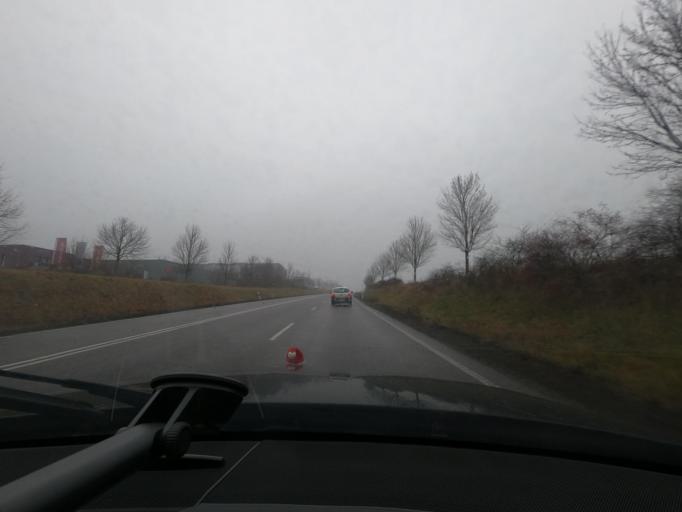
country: DE
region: Thuringia
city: Heilbad Heiligenstadt
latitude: 51.3901
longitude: 10.1305
